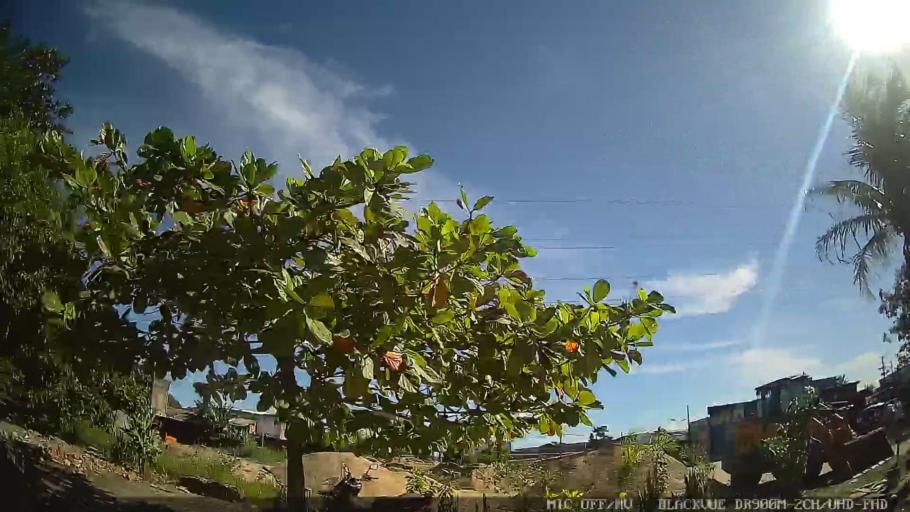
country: BR
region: Sao Paulo
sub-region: Santos
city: Santos
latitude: -23.9410
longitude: -46.2846
